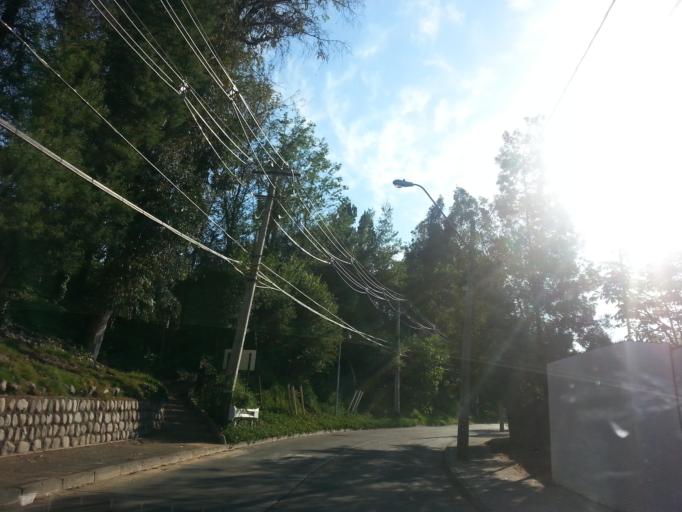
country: CL
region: Santiago Metropolitan
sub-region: Provincia de Santiago
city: Villa Presidente Frei, Nunoa, Santiago, Chile
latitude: -33.3854
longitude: -70.5198
